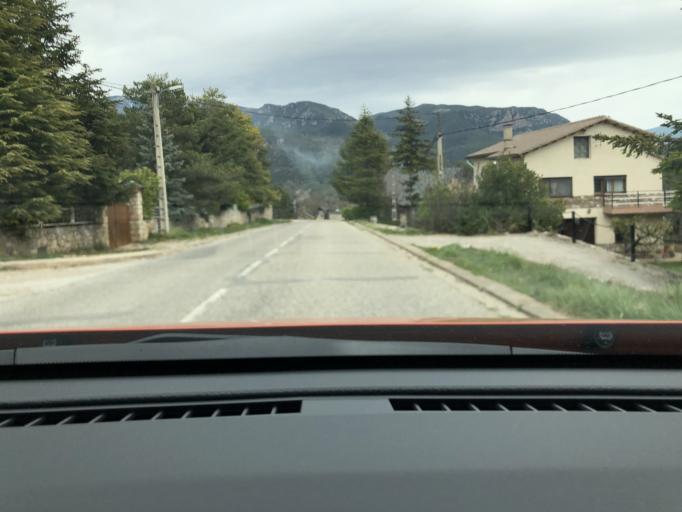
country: ES
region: Catalonia
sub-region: Provincia de Lleida
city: Gosol
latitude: 42.1376
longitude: 1.5836
